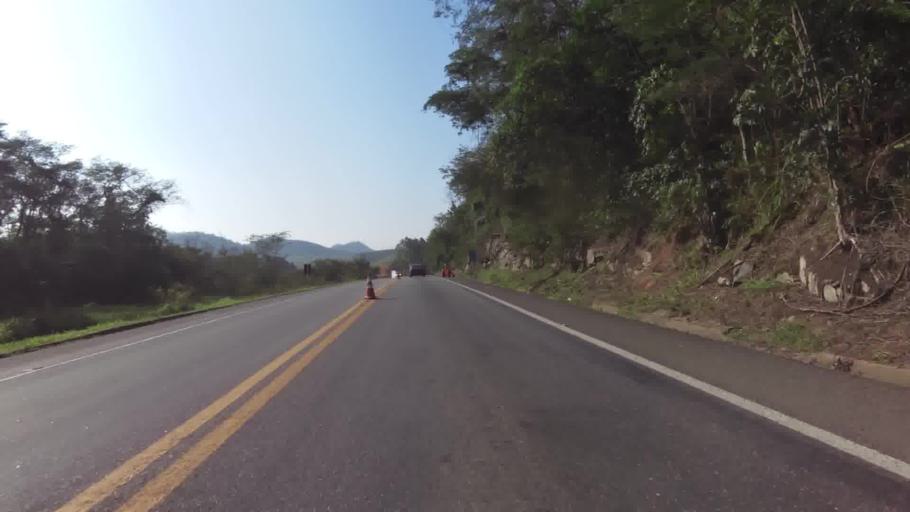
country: BR
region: Espirito Santo
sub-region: Iconha
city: Iconha
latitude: -20.7444
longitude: -40.7602
